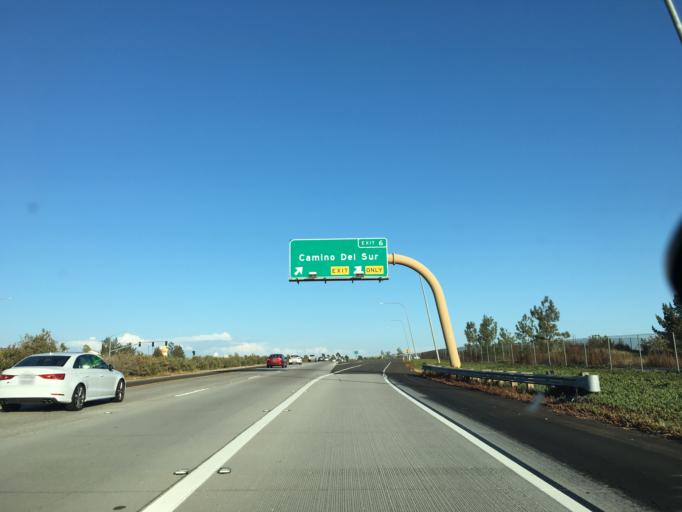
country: US
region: California
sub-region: San Diego County
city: Fairbanks Ranch
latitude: 32.9611
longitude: -117.1576
